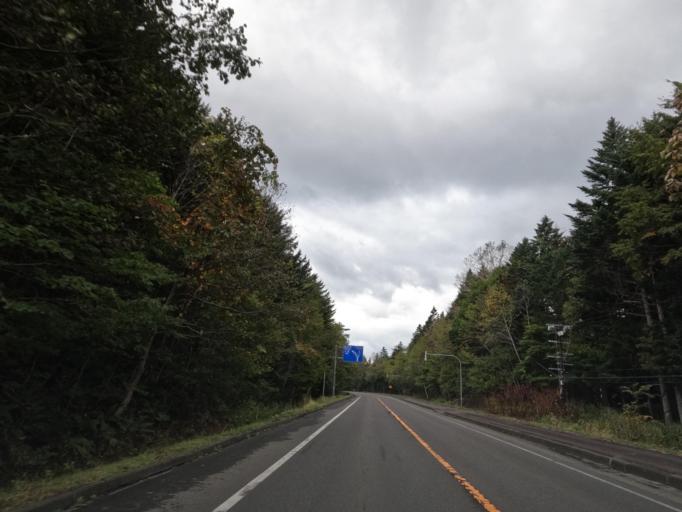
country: JP
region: Hokkaido
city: Shiraoi
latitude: 42.7490
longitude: 141.4161
